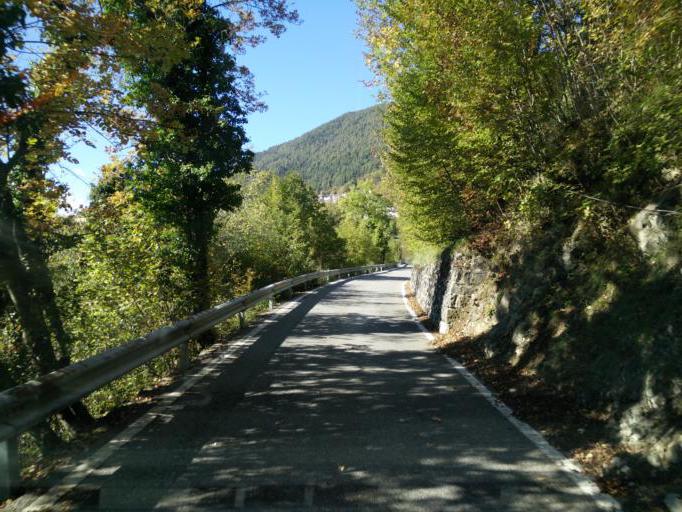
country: IT
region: Lombardy
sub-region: Provincia di Brescia
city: Capovalle
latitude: 45.7522
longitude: 10.5528
